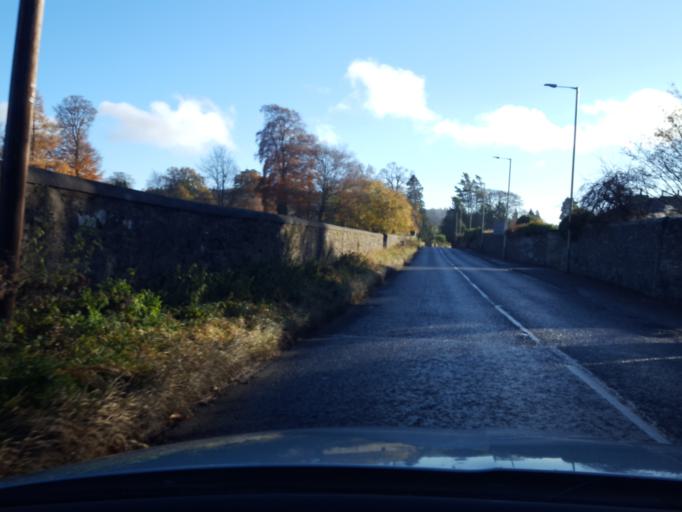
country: GB
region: Scotland
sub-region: Perth and Kinross
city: Perth
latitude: 56.4076
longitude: -3.4274
